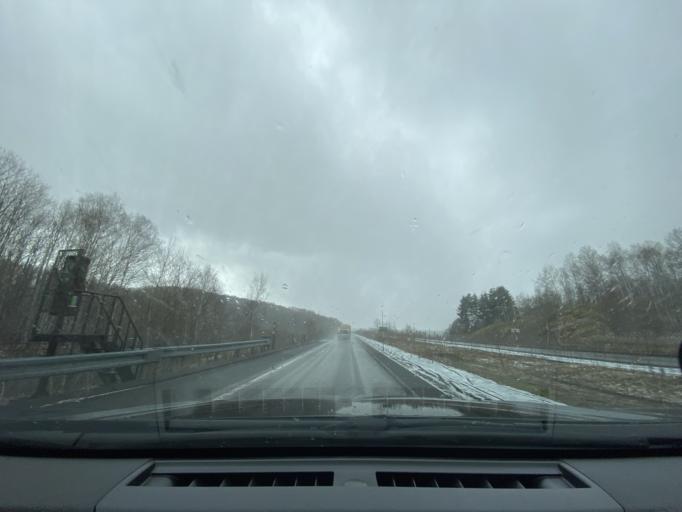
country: JP
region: Hokkaido
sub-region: Asahikawa-shi
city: Asahikawa
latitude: 43.8733
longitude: 142.4487
